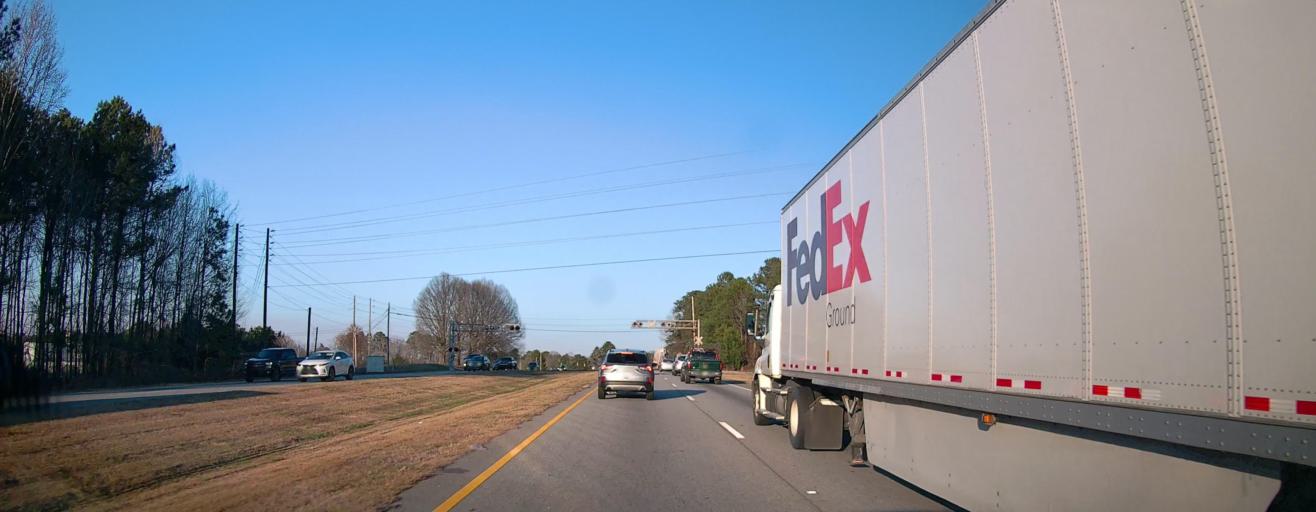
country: US
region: Georgia
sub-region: Fayette County
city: Tyrone
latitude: 33.4939
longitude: -84.5812
